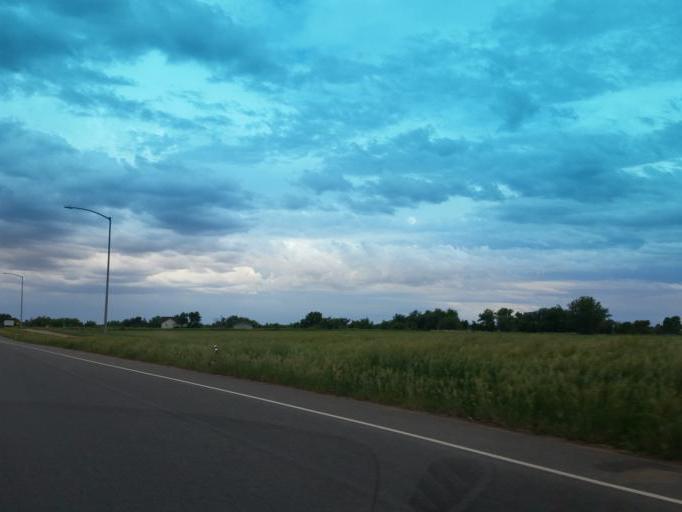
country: US
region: Colorado
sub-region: Larimer County
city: Fort Collins
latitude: 40.5515
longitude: -104.9995
